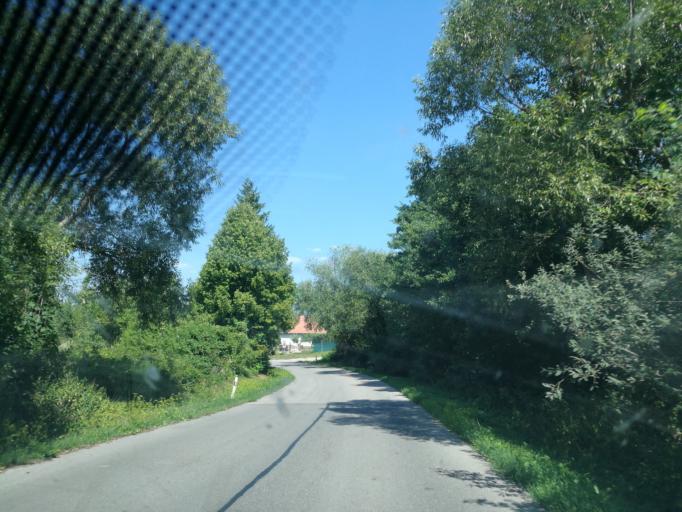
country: SK
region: Nitriansky
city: Banovce nad Bebravou
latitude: 48.7348
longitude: 18.1635
